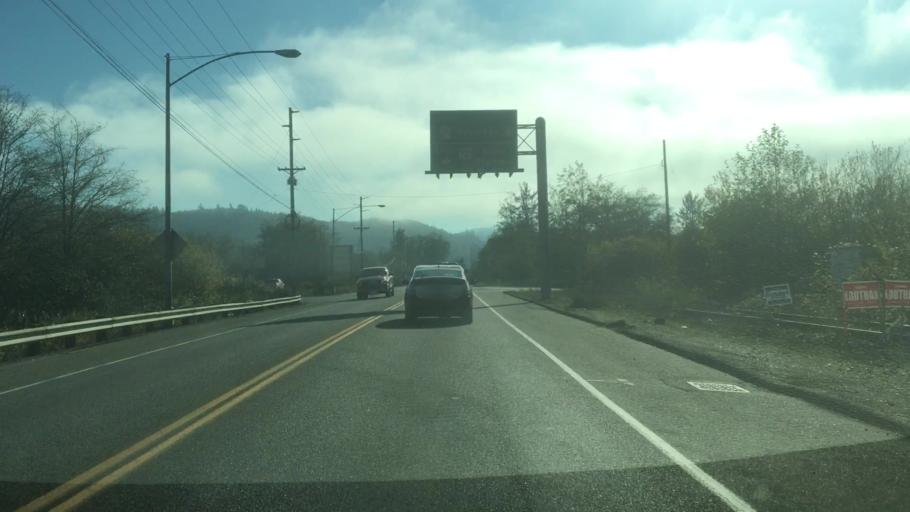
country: US
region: Washington
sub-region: Grays Harbor County
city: Montesano
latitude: 46.9754
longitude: -123.6010
